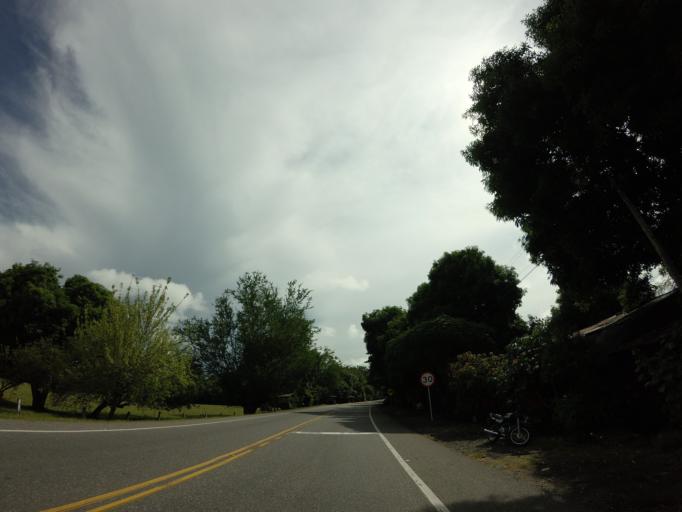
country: CO
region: Tolima
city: Honda
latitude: 5.3373
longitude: -74.7396
